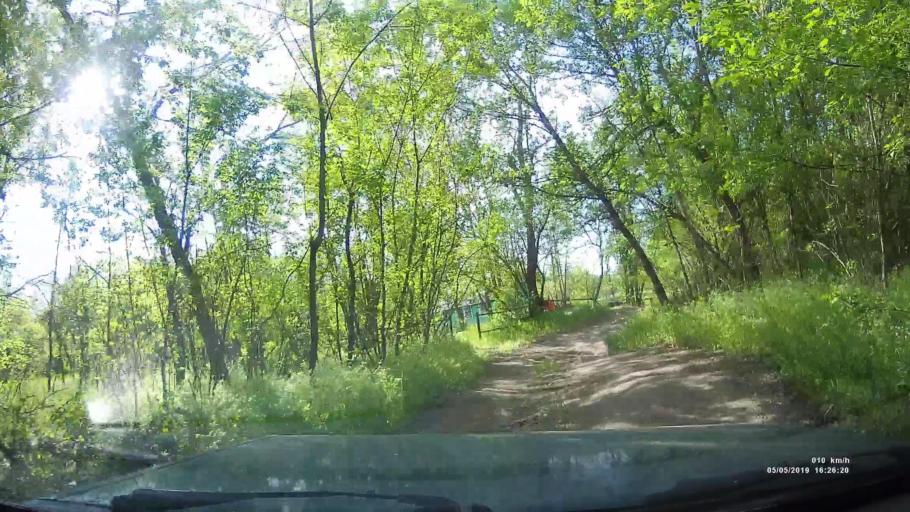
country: RU
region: Rostov
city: Ust'-Donetskiy
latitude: 47.7628
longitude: 41.0215
